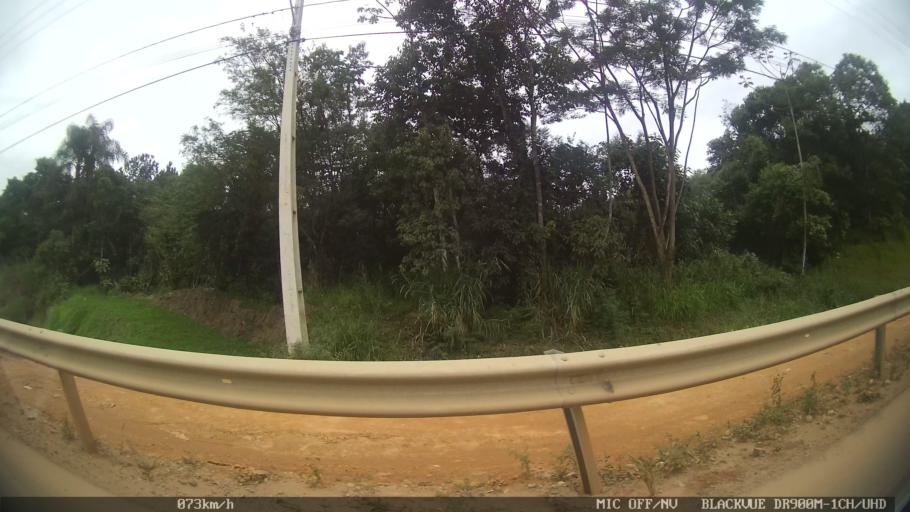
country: BR
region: Santa Catarina
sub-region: Joinville
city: Joinville
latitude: -26.2567
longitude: -48.8772
